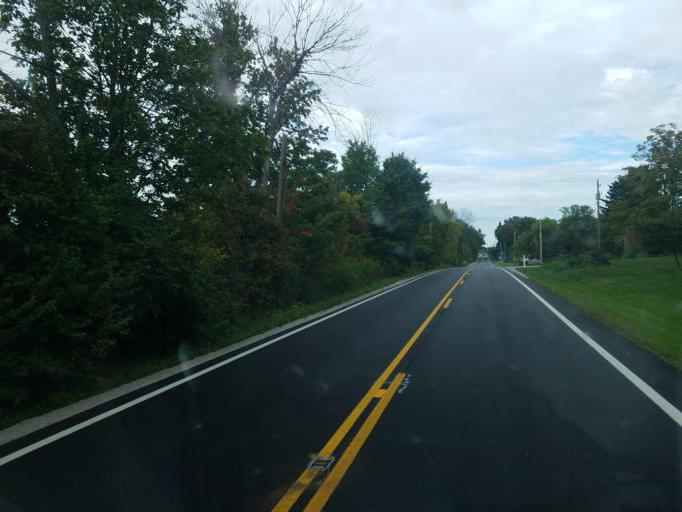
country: US
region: Ohio
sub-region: Franklin County
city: New Albany
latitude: 40.1171
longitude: -82.8109
